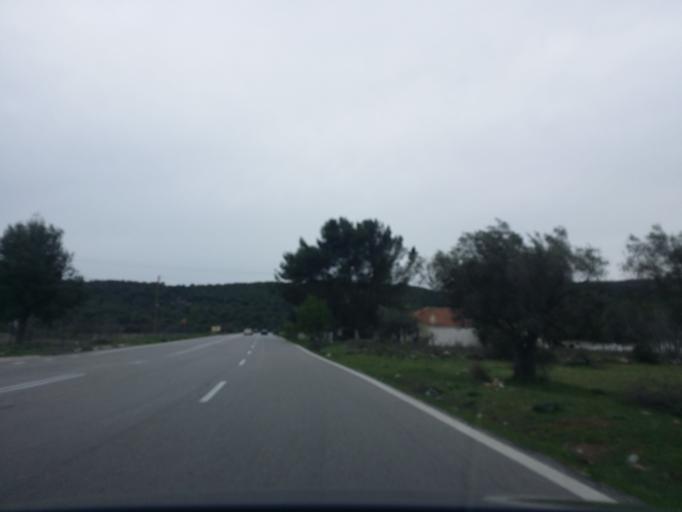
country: GR
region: Attica
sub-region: Nomarchia Dytikis Attikis
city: Vilia
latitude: 38.1472
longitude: 23.4230
